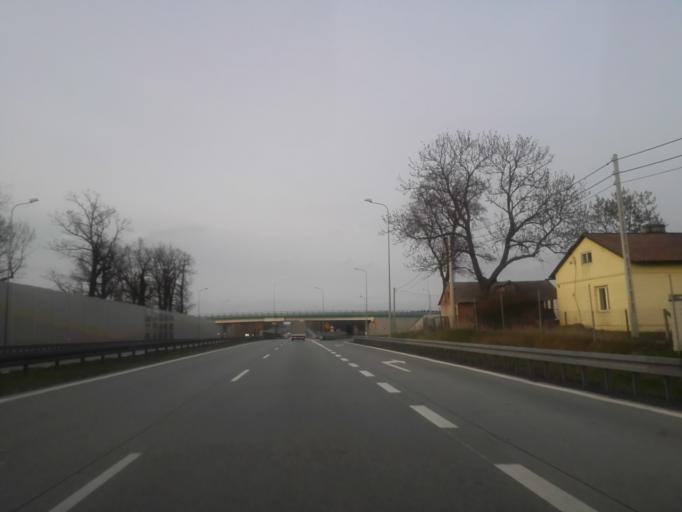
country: PL
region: Lodz Voivodeship
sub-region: Powiat rawski
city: Rawa Mazowiecka
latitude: 51.8022
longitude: 20.2993
